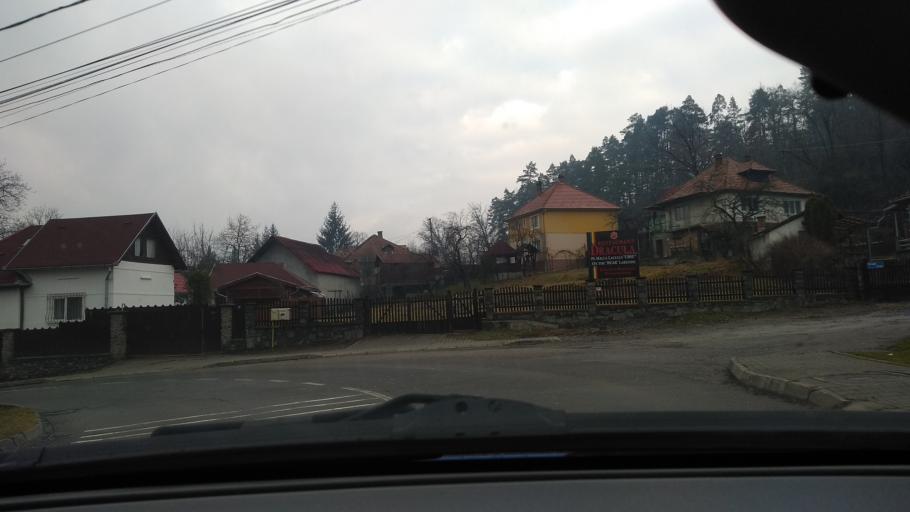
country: RO
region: Mures
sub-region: Oras Sovata
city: Sovata
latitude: 46.5981
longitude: 25.0749
